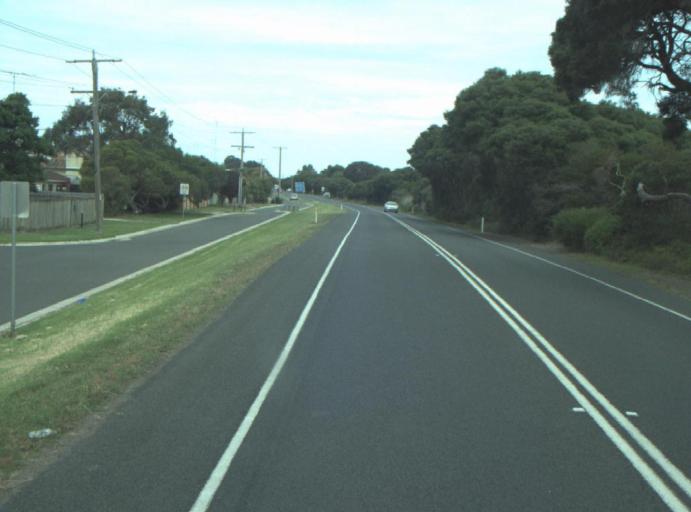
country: AU
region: Victoria
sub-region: Greater Geelong
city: Leopold
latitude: -38.2556
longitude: 144.5041
